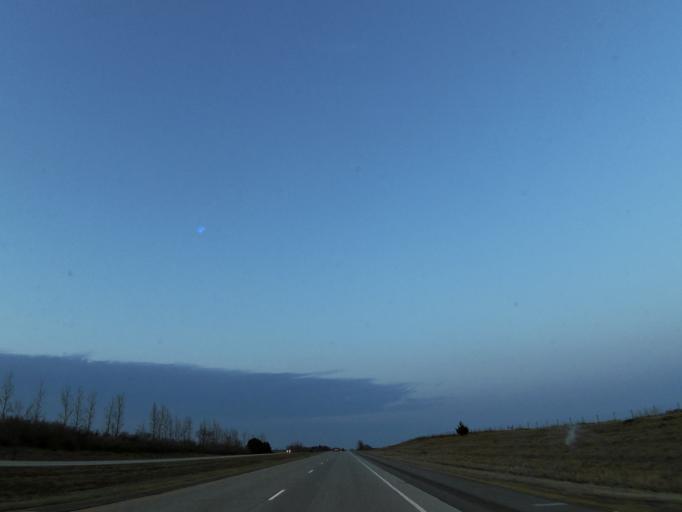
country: US
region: Minnesota
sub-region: Mower County
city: Grand Meadow
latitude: 43.7764
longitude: -92.6241
